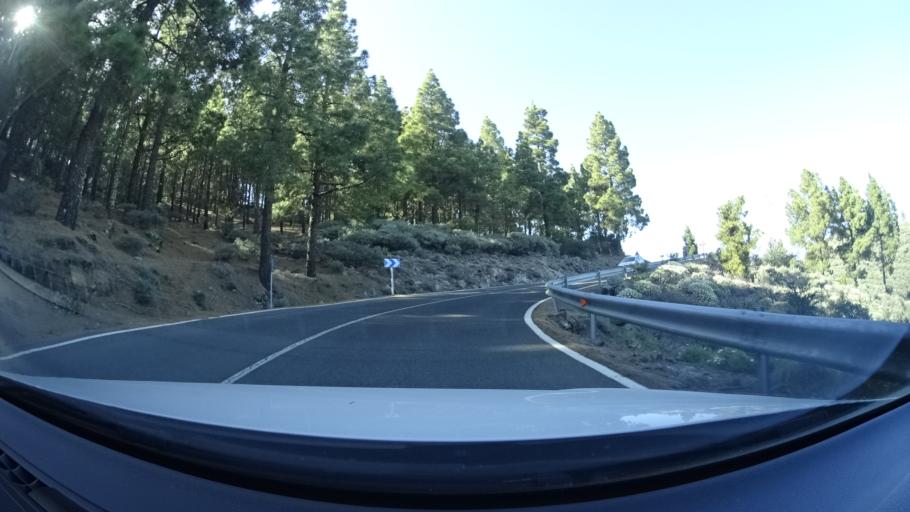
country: ES
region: Canary Islands
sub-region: Provincia de Las Palmas
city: Vega de San Mateo
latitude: 27.9640
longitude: -15.5395
